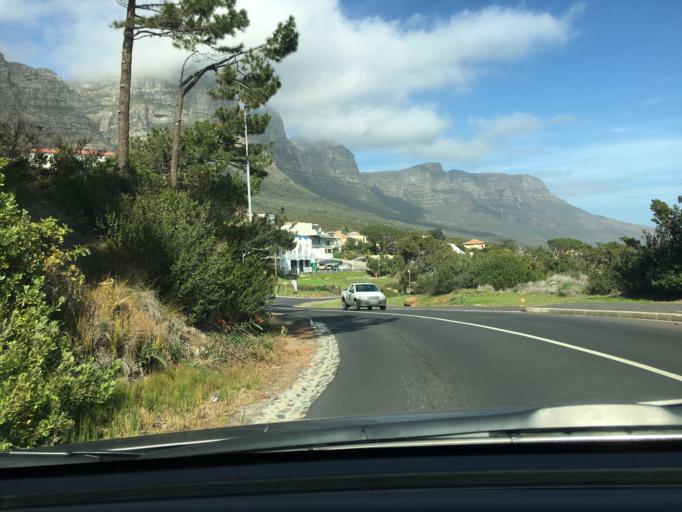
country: ZA
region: Western Cape
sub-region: City of Cape Town
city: Cape Town
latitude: -33.9619
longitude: 18.3798
